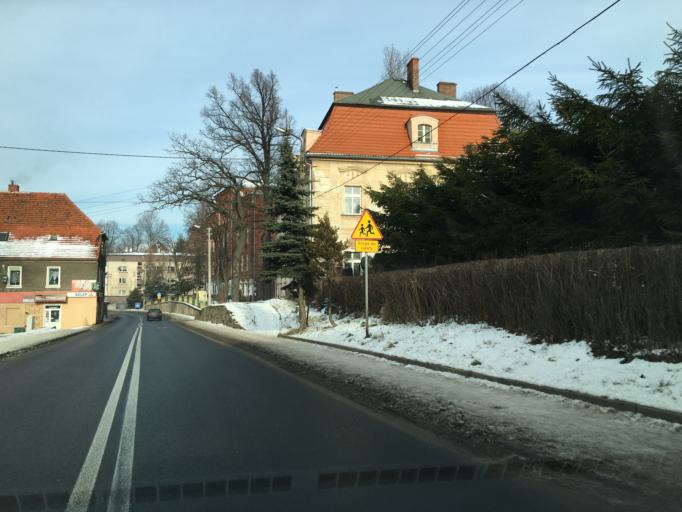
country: PL
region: Lower Silesian Voivodeship
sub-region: Powiat walbrzyski
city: Gluszyca
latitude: 50.6807
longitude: 16.3788
